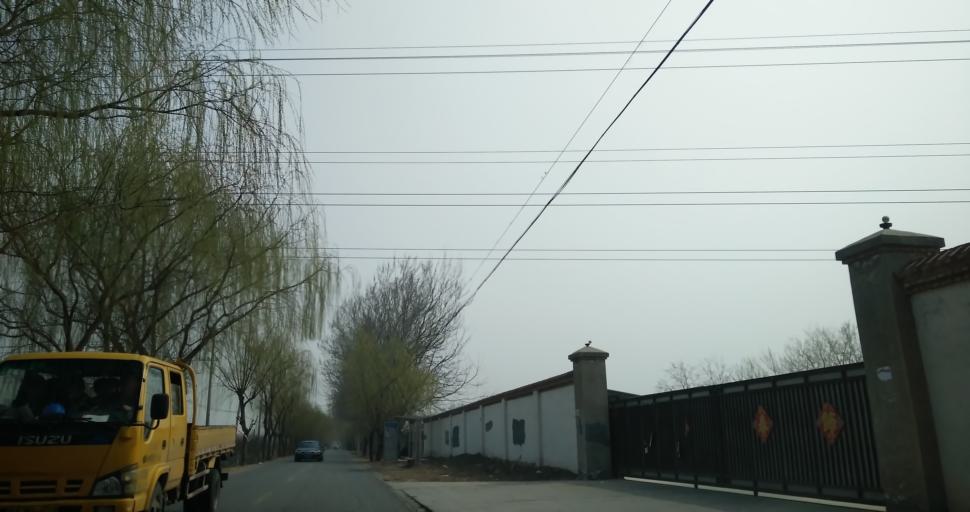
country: CN
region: Beijing
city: Qingyundian
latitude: 39.6985
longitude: 116.4978
